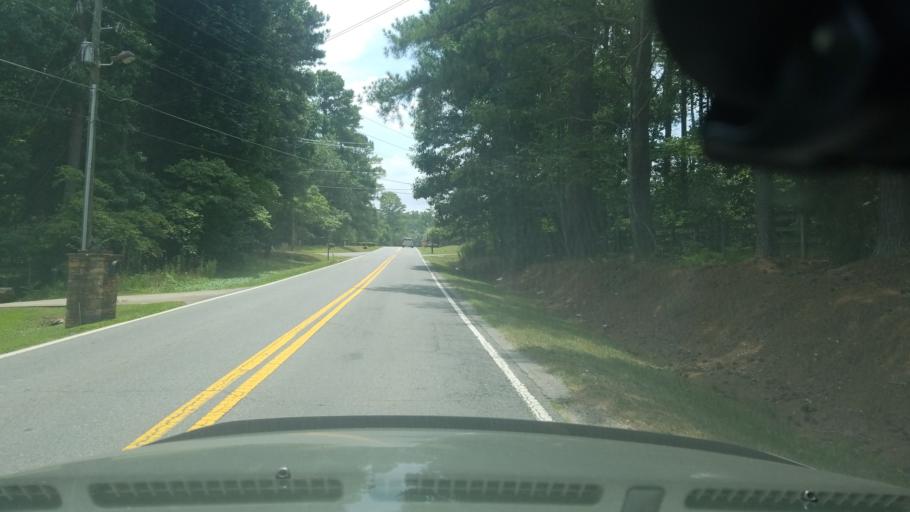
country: US
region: Georgia
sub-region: Fulton County
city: Milton
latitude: 34.1758
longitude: -84.2728
